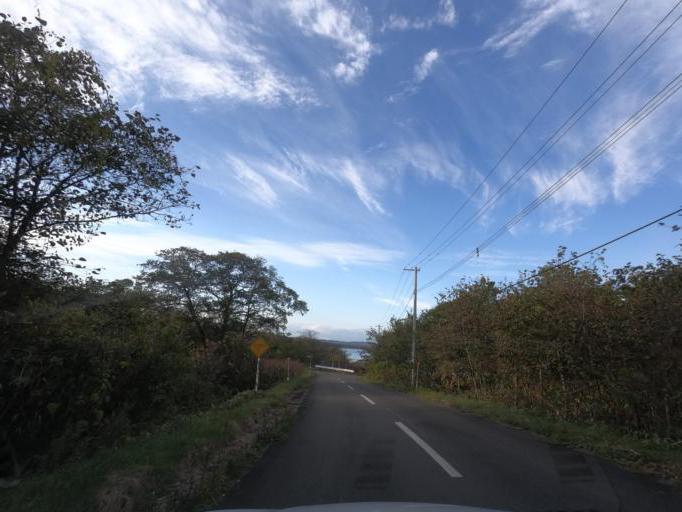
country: JP
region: Hokkaido
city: Obihiro
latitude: 42.5454
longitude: 143.4935
